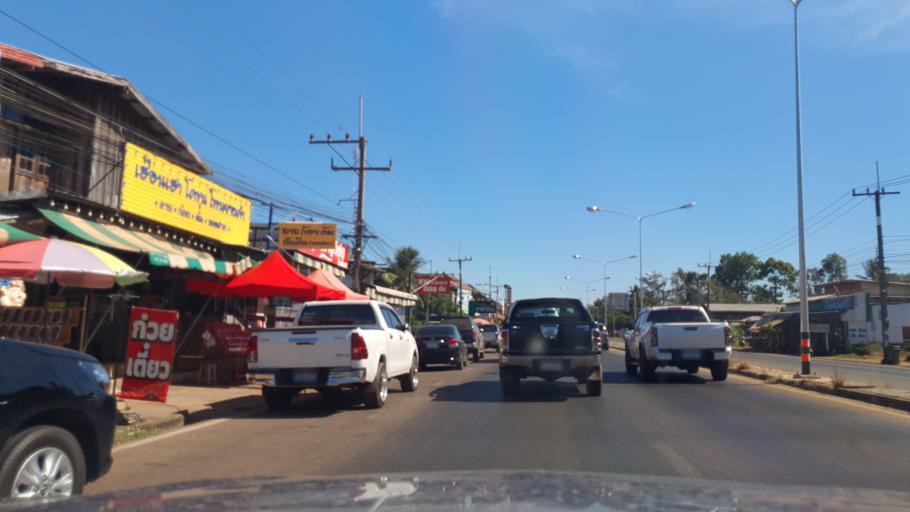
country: TH
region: Sakon Nakhon
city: Tao Ngoi
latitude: 17.0829
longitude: 104.1910
